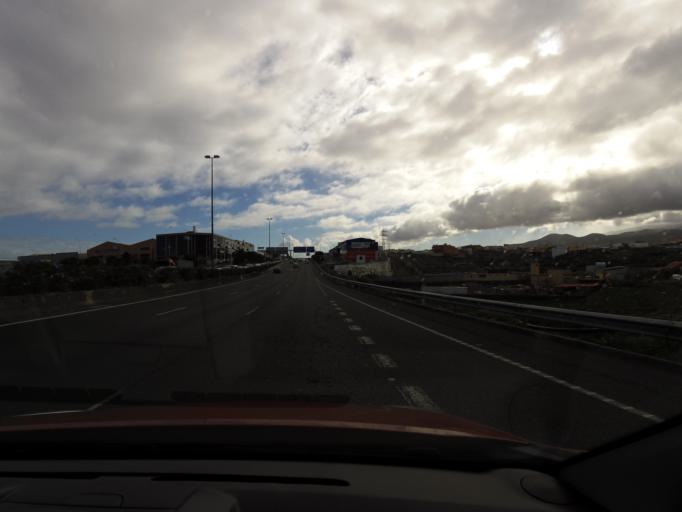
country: ES
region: Canary Islands
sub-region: Provincia de Las Palmas
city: Telde
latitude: 28.0020
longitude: -15.3919
